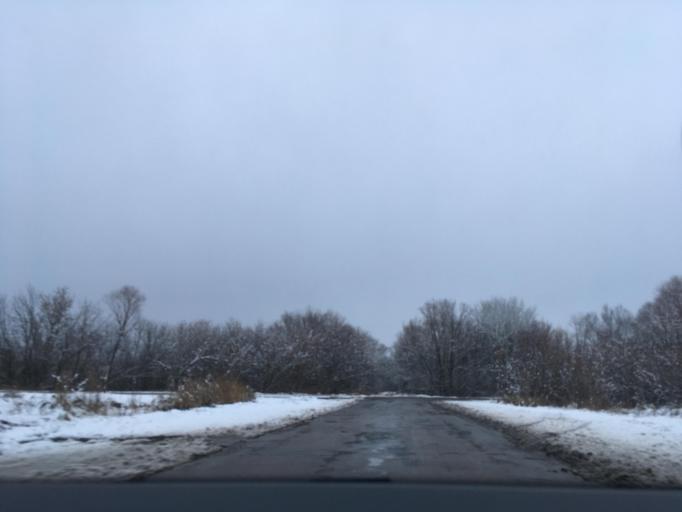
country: RU
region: Voronezj
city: Mitrofanovka
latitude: 50.1342
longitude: 39.9911
